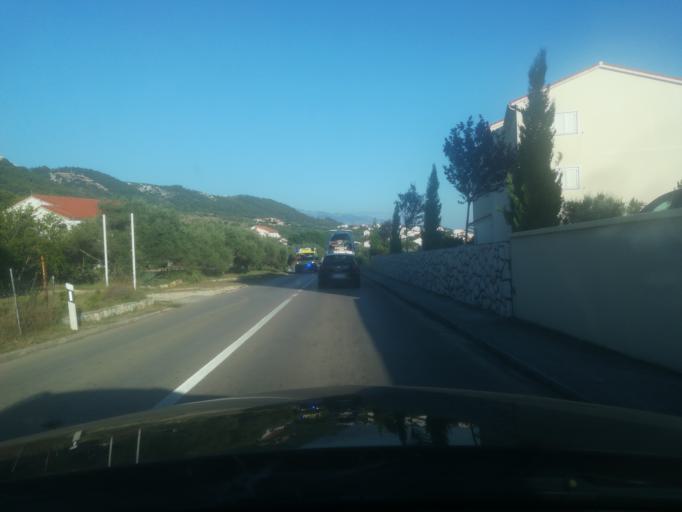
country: HR
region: Primorsko-Goranska
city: Banjol
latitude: 44.7515
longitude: 14.7833
